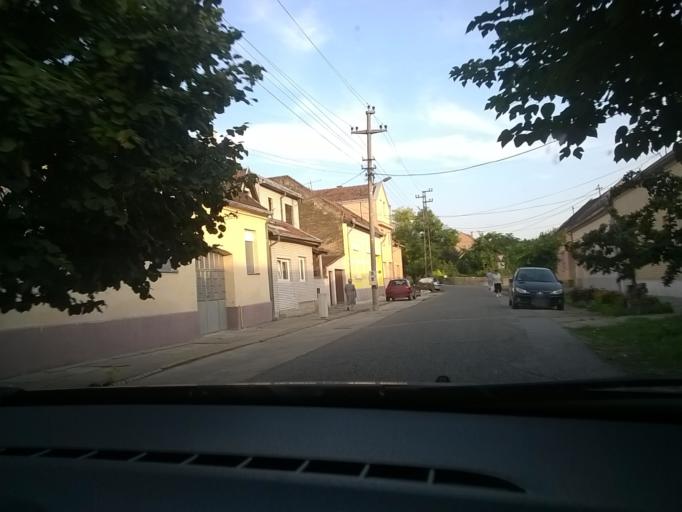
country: RS
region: Autonomna Pokrajina Vojvodina
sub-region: Juznobanatski Okrug
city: Vrsac
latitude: 45.1209
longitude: 21.2913
